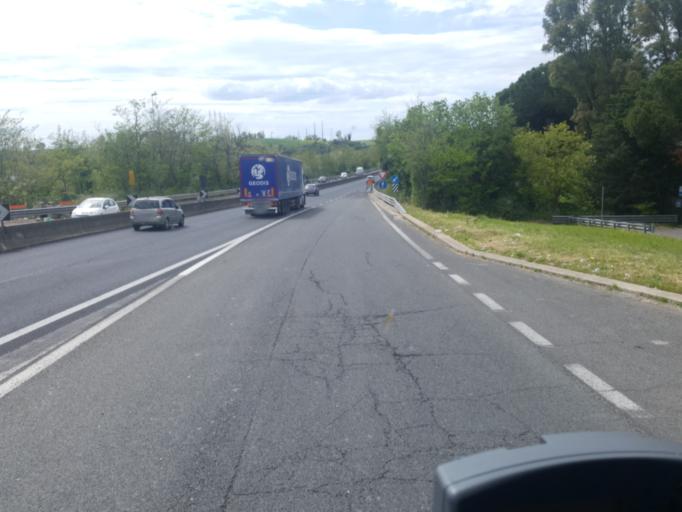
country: IT
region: Latium
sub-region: Citta metropolitana di Roma Capitale
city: La Massimina-Casal Lumbroso
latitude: 41.8829
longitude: 12.3414
